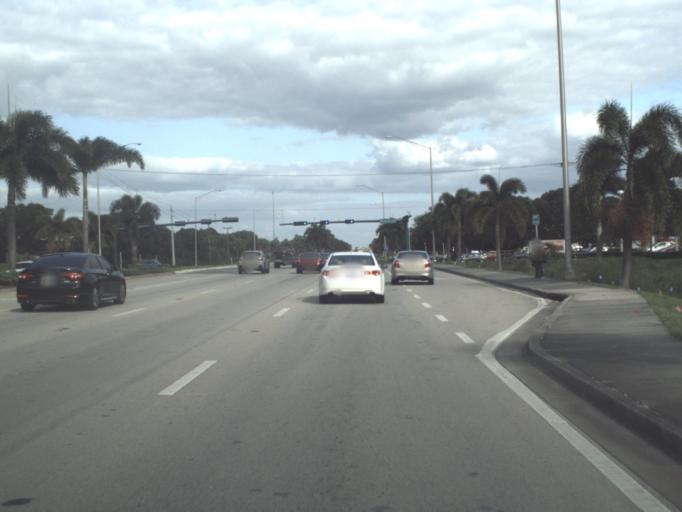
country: US
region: Florida
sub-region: Collier County
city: Vineyards
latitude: 26.2114
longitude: -81.7449
